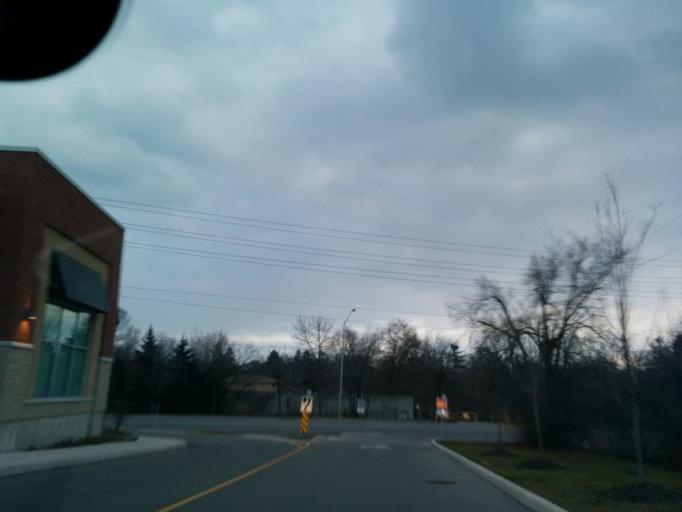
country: CA
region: Ontario
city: Oakville
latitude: 43.4611
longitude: -79.6748
